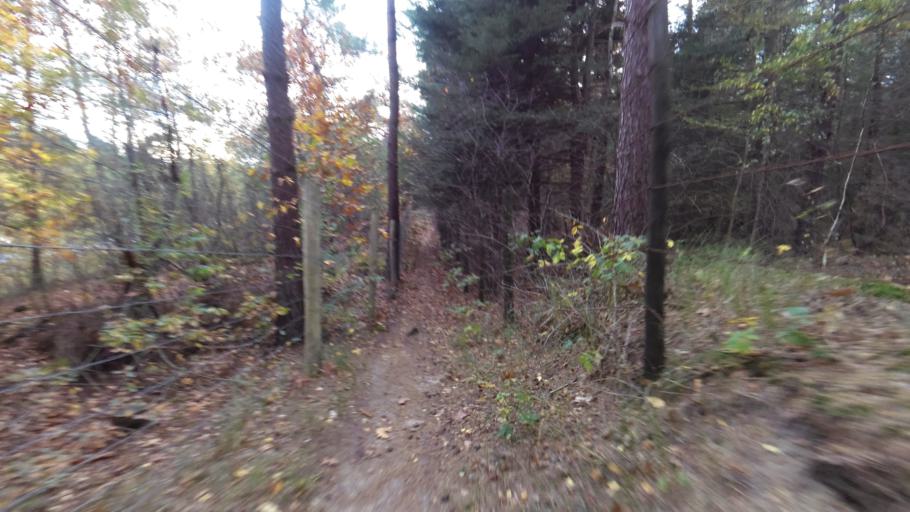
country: NL
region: Gelderland
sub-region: Gemeente Oldebroek
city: Oldebroek
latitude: 52.4274
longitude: 5.9288
